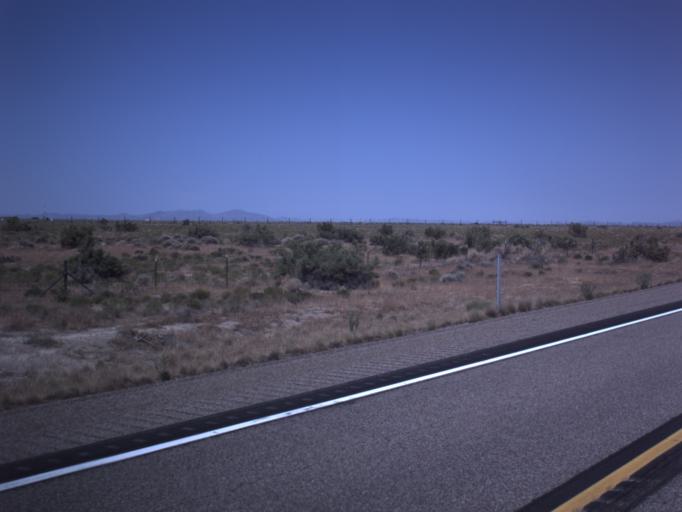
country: US
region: Utah
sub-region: Millard County
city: Delta
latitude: 39.3867
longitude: -112.4978
